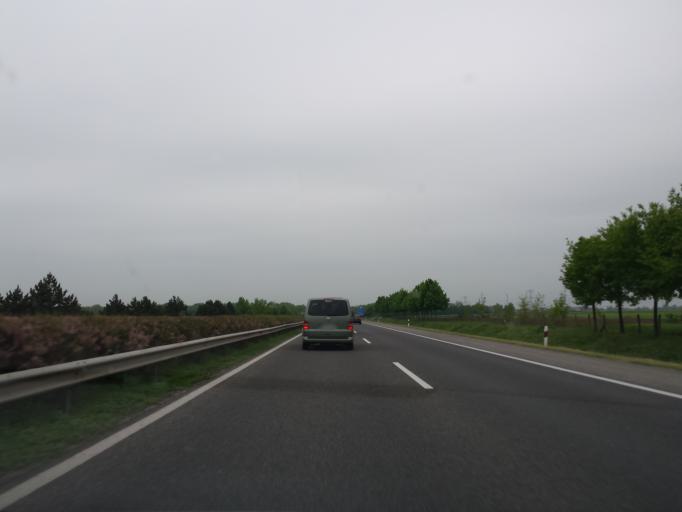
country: HU
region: Gyor-Moson-Sopron
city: Mosonszentmiklos
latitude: 47.7393
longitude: 17.4330
